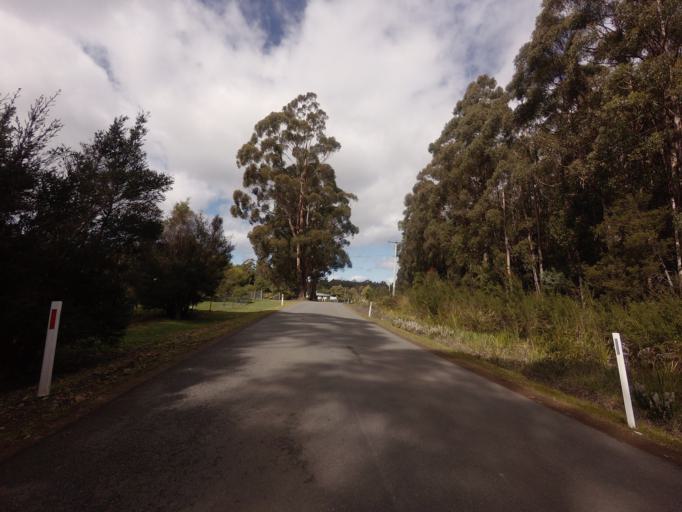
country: AU
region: Tasmania
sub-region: Huon Valley
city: Geeveston
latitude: -43.4206
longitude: 146.9710
